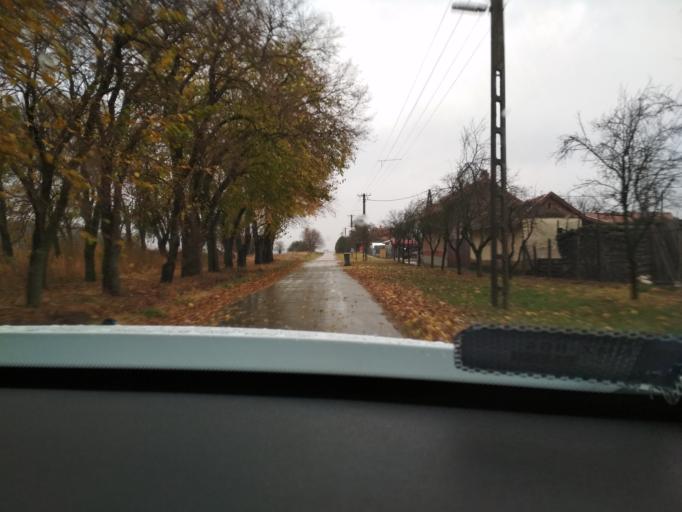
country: HU
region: Csongrad
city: Opusztaszer
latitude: 46.4342
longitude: 20.1411
